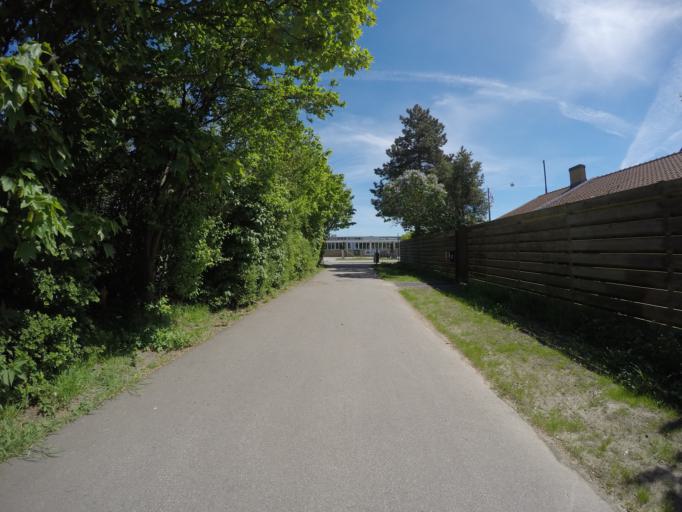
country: SE
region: Skane
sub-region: Malmo
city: Bunkeflostrand
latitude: 55.5614
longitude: 12.9190
